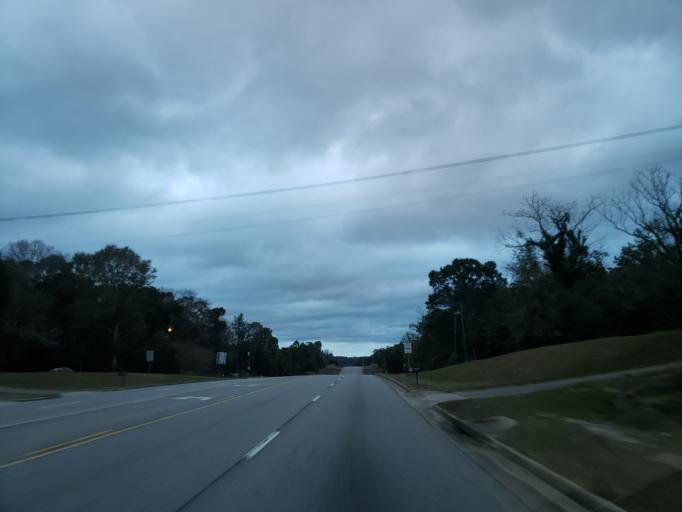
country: US
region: Alabama
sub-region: Mobile County
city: Chickasaw
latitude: 30.7957
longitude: -88.2254
